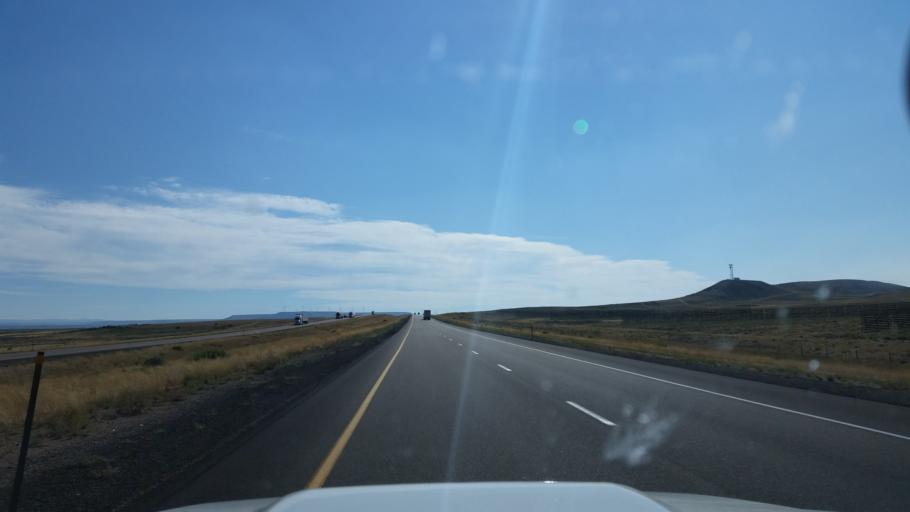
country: US
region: Wyoming
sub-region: Uinta County
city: Lyman
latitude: 41.3521
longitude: -110.3765
